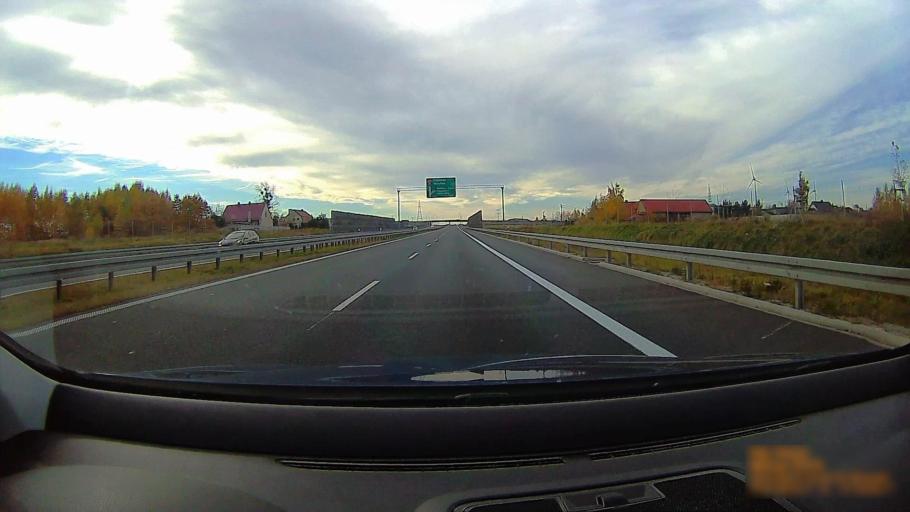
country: PL
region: Greater Poland Voivodeship
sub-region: Powiat ostrowski
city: Przygodzice
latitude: 51.6364
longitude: 17.8733
